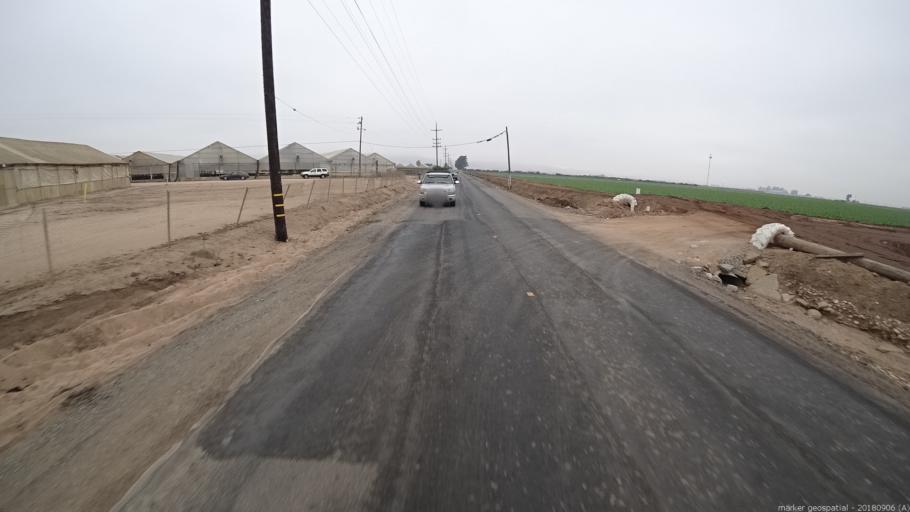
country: US
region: California
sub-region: Monterey County
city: Chualar
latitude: 36.6199
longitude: -121.5559
